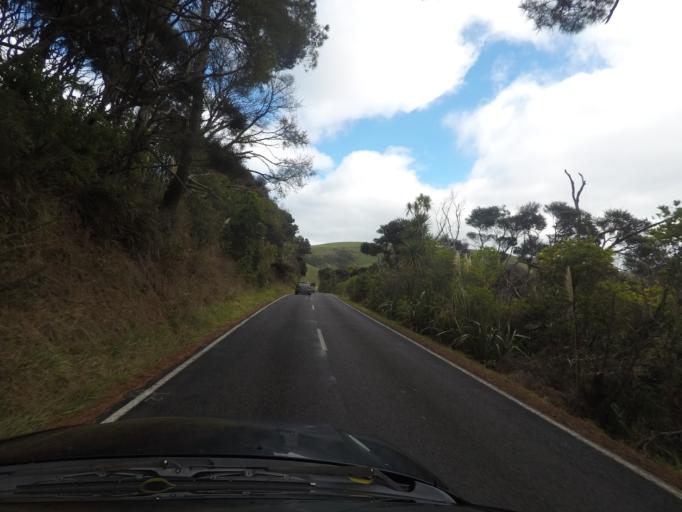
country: NZ
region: Auckland
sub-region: Auckland
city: Muriwai Beach
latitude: -36.8771
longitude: 174.4546
